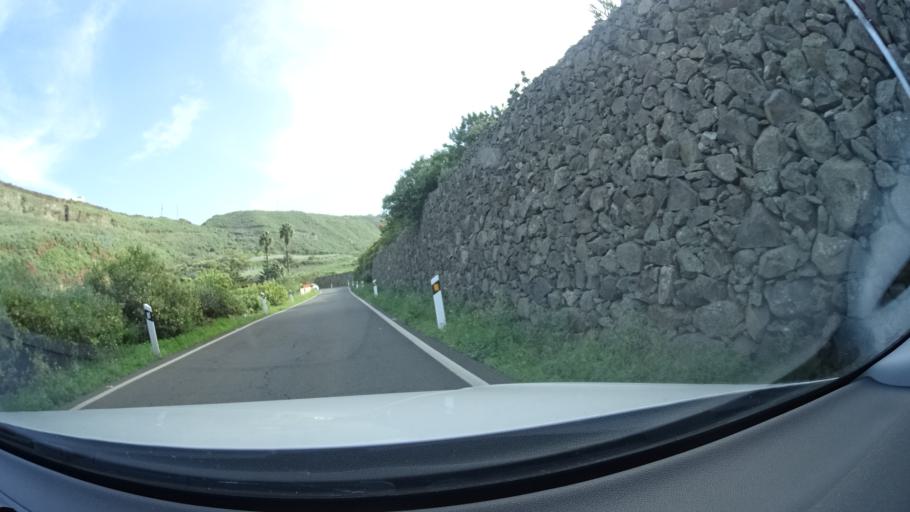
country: ES
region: Canary Islands
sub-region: Provincia de Las Palmas
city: Guia
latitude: 28.1094
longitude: -15.6416
